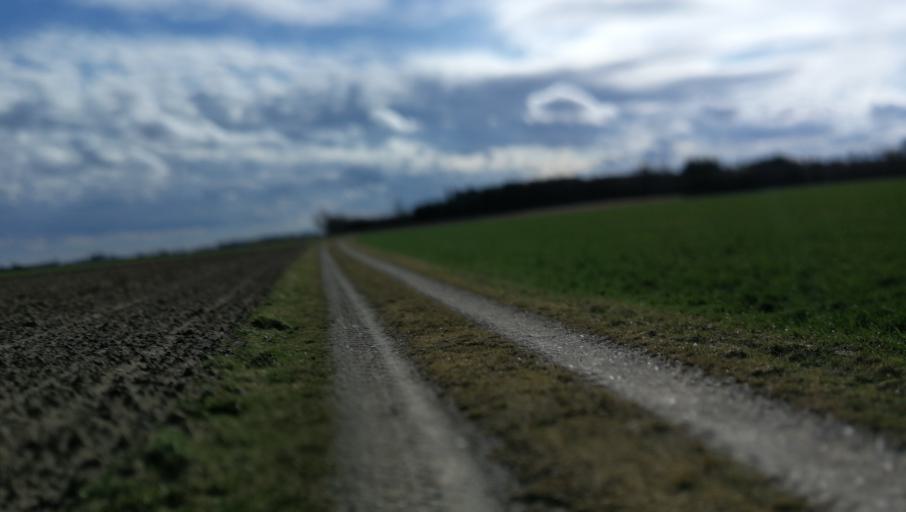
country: DE
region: Bavaria
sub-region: Upper Bavaria
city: Fuerstenfeldbruck
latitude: 48.2050
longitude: 11.2107
